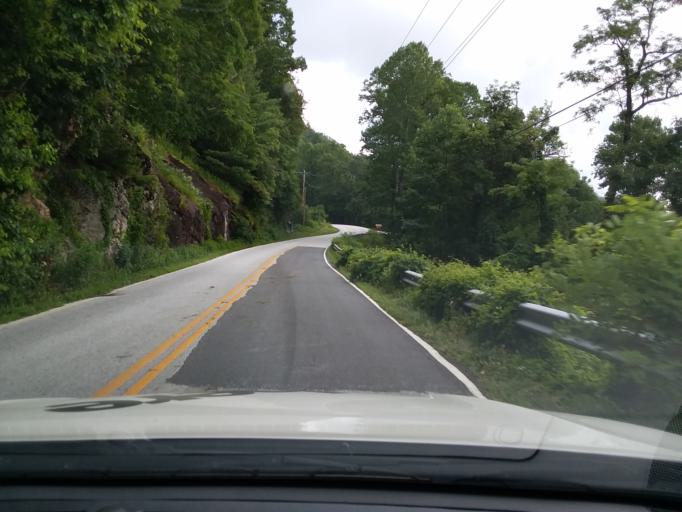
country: US
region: Georgia
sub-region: Rabun County
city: Mountain City
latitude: 35.0302
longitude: -83.2747
